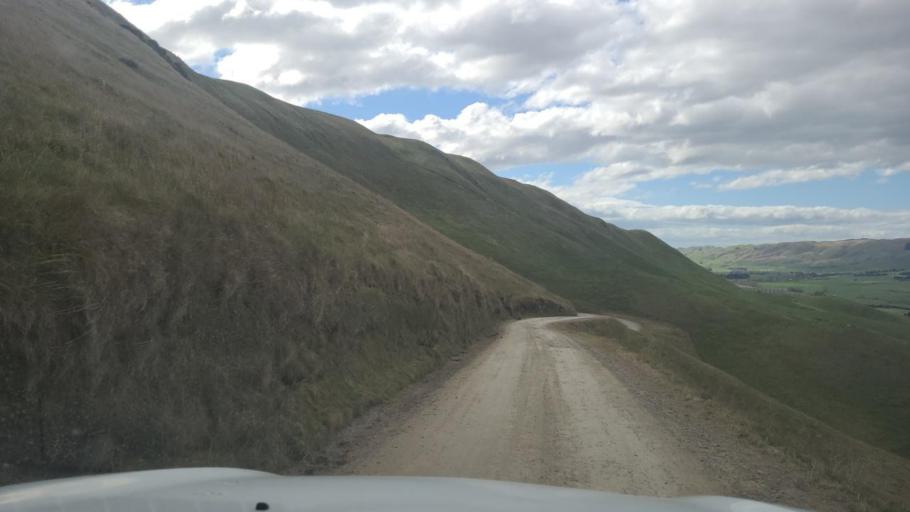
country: NZ
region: Hawke's Bay
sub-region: Hastings District
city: Hastings
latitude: -39.7526
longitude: 176.6881
